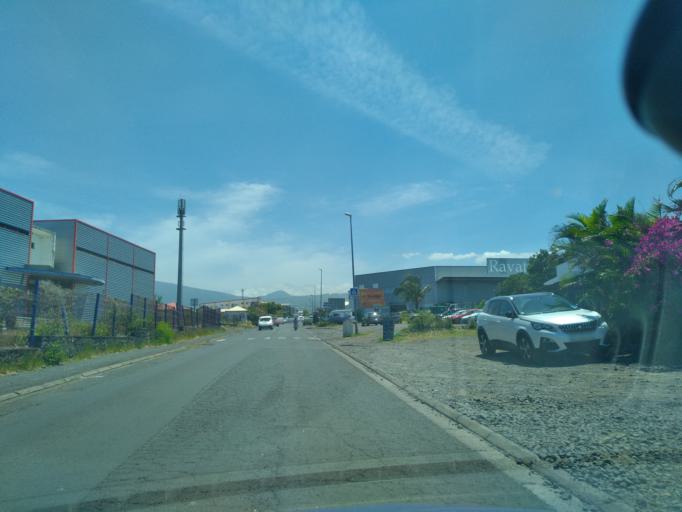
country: RE
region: Reunion
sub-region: Reunion
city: Saint-Pierre
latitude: -21.3199
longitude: 55.4511
